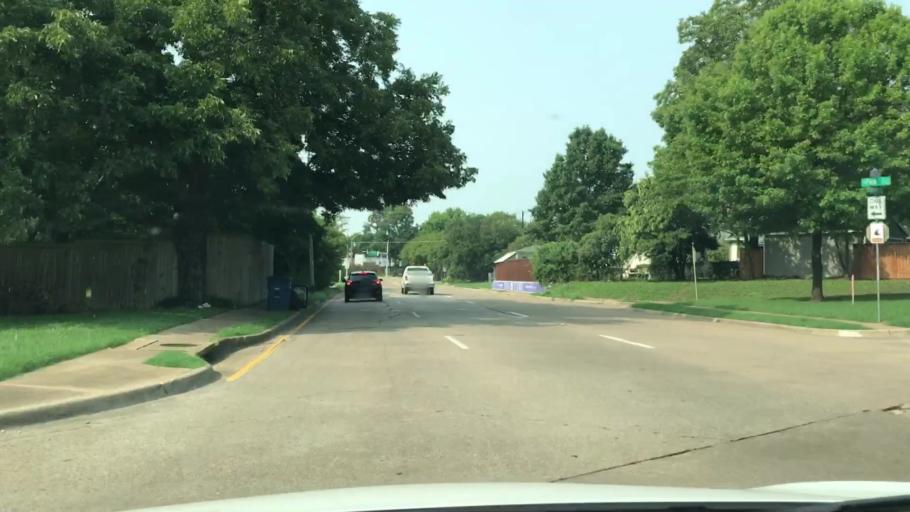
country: US
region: Texas
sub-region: Dallas County
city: Dallas
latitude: 32.7515
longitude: -96.8379
